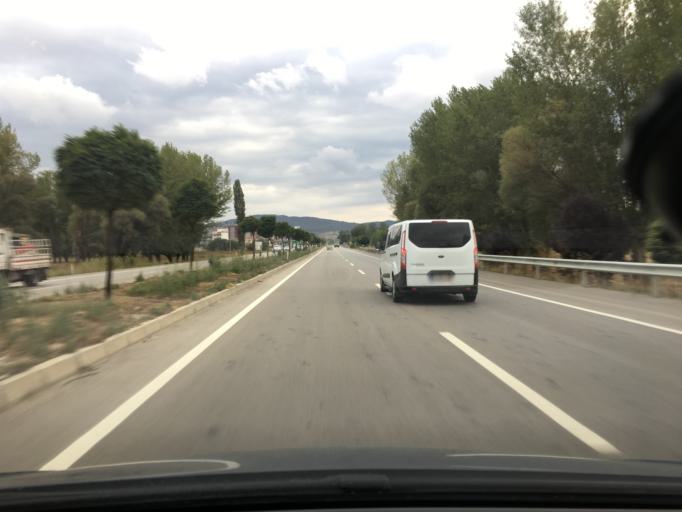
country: TR
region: Afyonkarahisar
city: Sincanli
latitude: 38.7505
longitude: 30.3577
